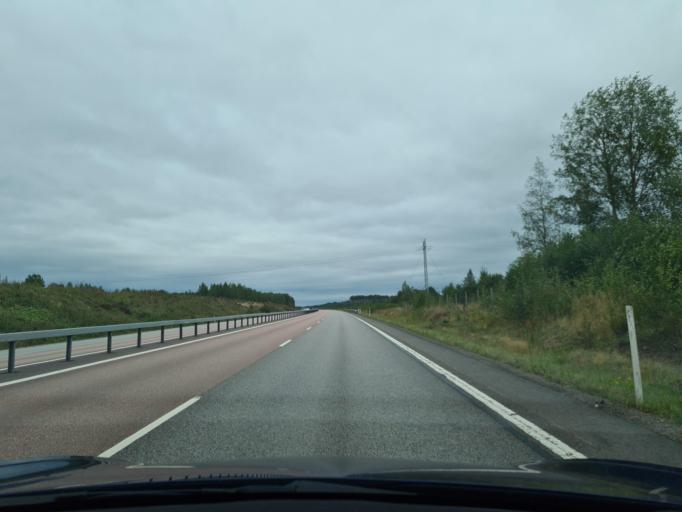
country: FI
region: South Karelia
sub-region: Lappeenranta
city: Lemi
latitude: 60.9452
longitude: 27.7631
